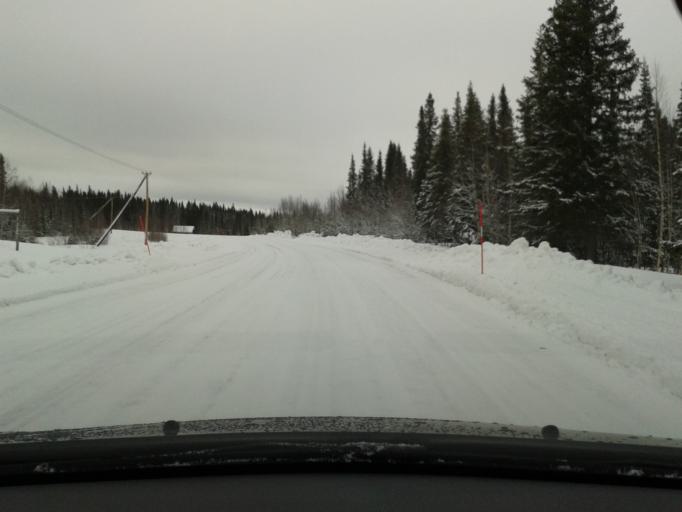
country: SE
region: Vaesterbotten
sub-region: Vilhelmina Kommun
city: Sjoberg
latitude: 65.2247
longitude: 15.9414
